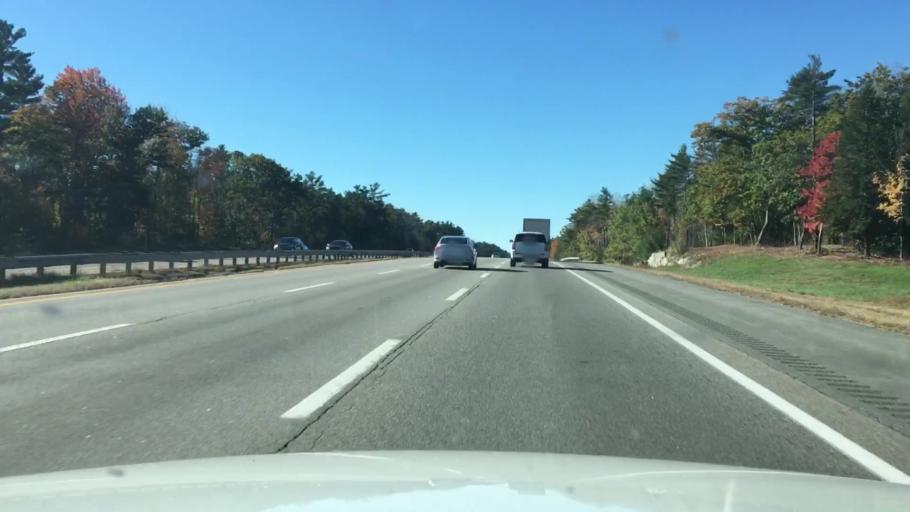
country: US
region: Maine
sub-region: Cumberland County
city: West Scarborough
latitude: 43.5708
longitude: -70.4073
